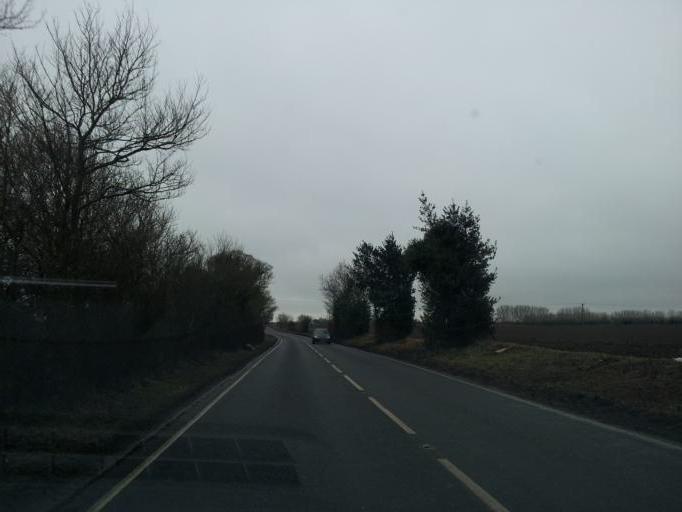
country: GB
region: England
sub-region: Essex
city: Manningtree
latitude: 51.9376
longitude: 1.0626
